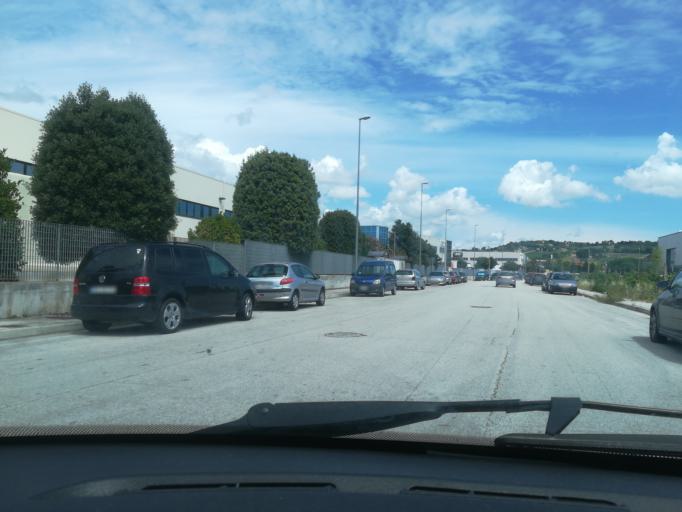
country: IT
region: The Marches
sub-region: Provincia di Macerata
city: Santa Maria Apparente
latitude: 43.2852
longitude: 13.6806
